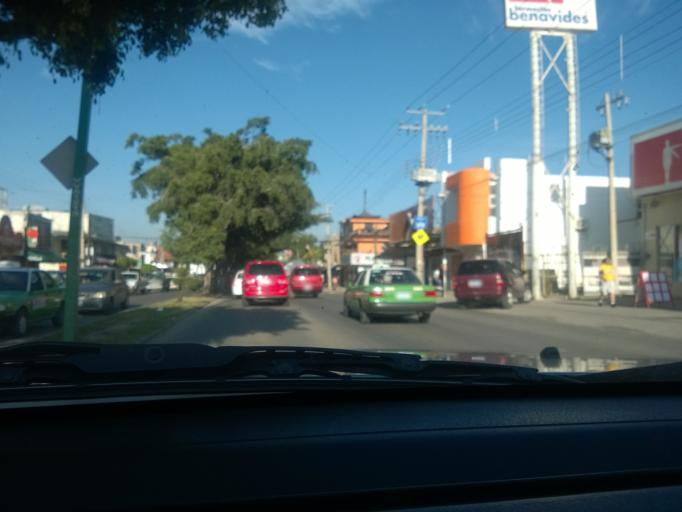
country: MX
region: Guanajuato
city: Leon
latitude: 21.1294
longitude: -101.6510
